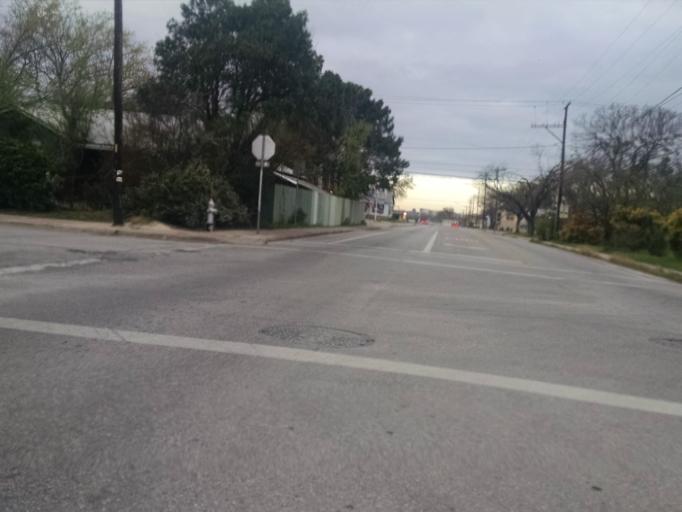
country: US
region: Texas
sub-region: Travis County
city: Austin
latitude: 30.3164
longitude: -97.7184
